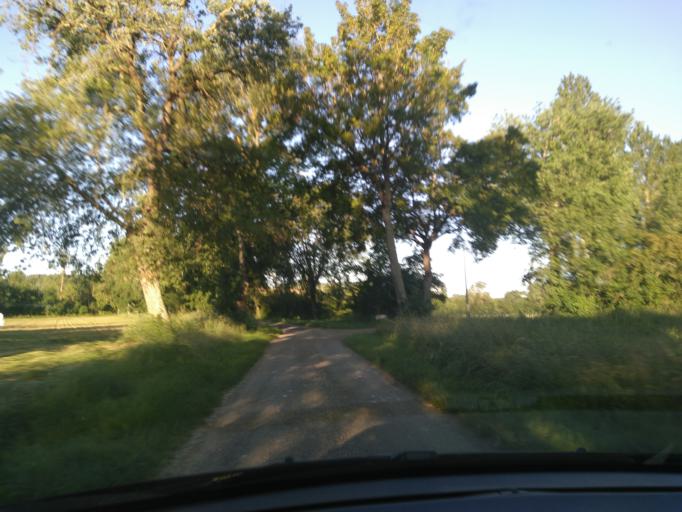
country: FR
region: Midi-Pyrenees
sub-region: Departement du Gers
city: Valence-sur-Baise
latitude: 43.8692
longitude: 0.4519
